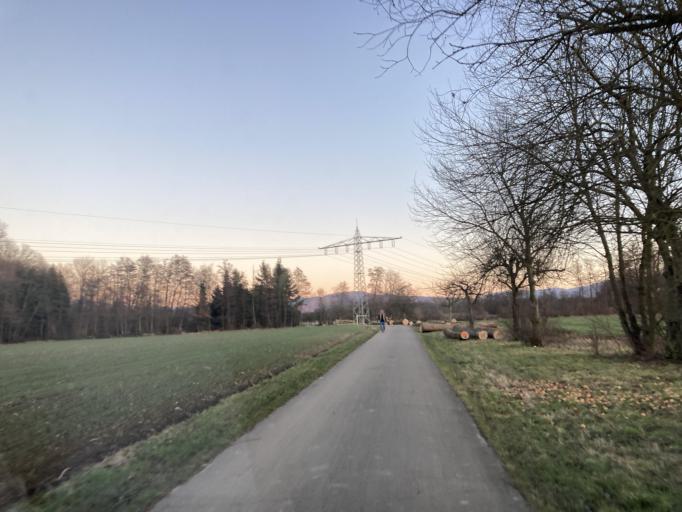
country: DE
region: Baden-Wuerttemberg
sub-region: Freiburg Region
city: Umkirch
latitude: 48.0465
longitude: 7.7693
